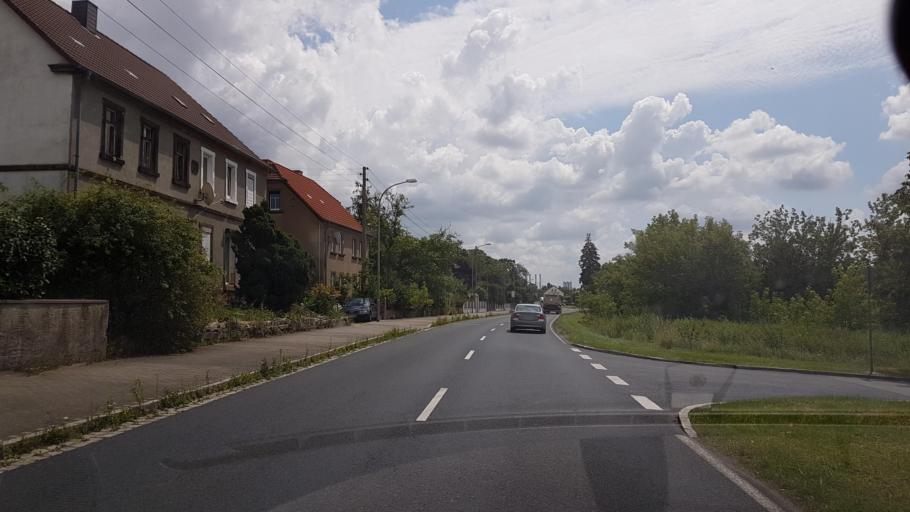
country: DE
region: Saxony
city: Nunchritz
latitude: 51.3038
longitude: 13.3797
